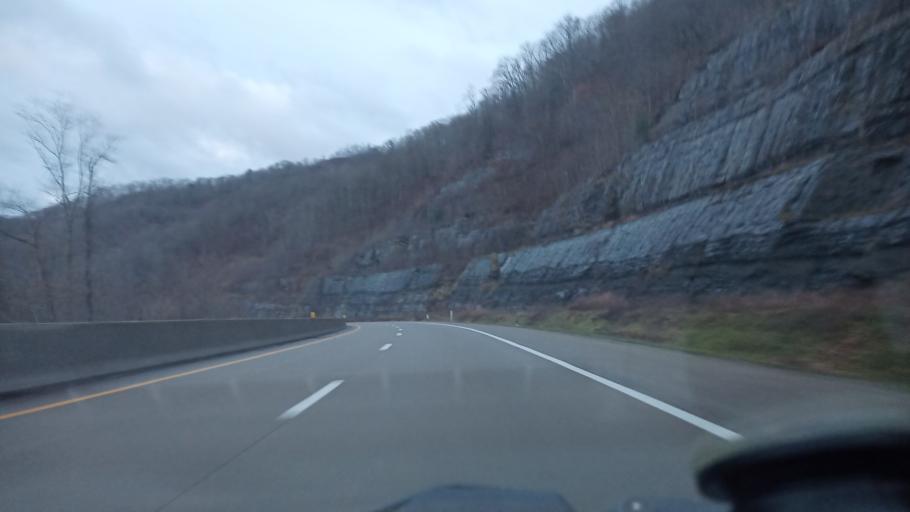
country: US
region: West Virginia
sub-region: Logan County
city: Mallory
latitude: 37.7628
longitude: -81.9168
